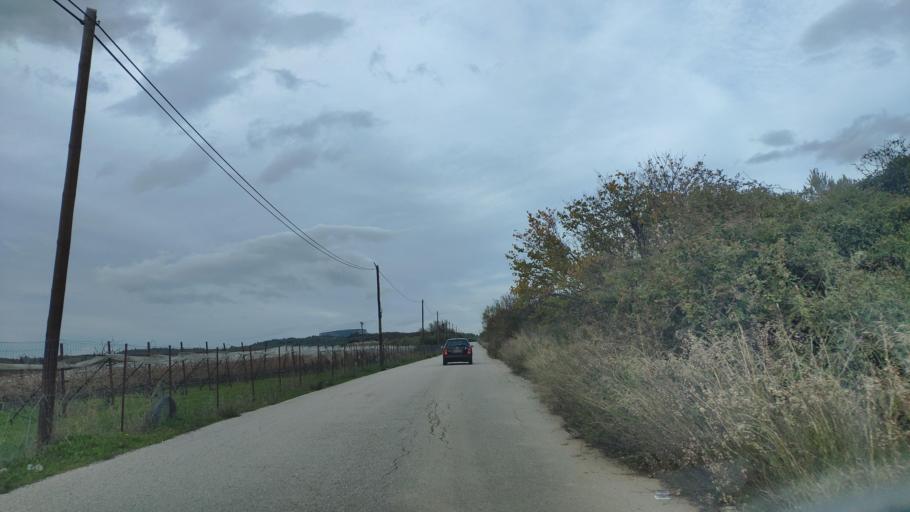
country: GR
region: Peloponnese
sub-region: Nomos Korinthias
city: Nemea
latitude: 37.7983
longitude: 22.7263
